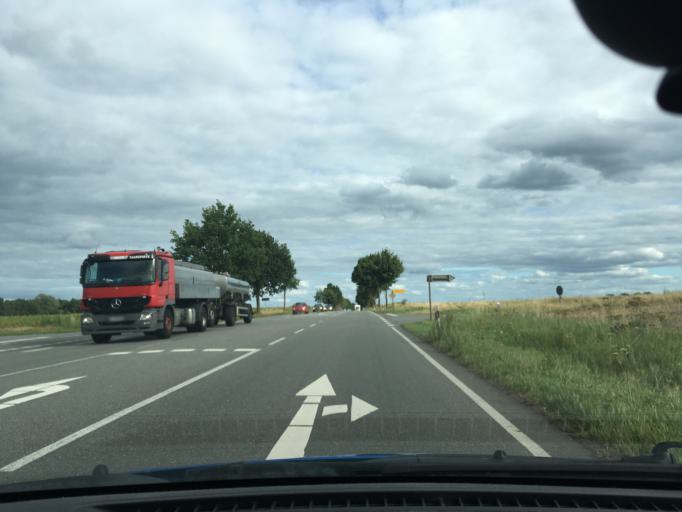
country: DE
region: Lower Saxony
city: Neu Wulmstorf
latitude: 53.4411
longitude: 9.7634
